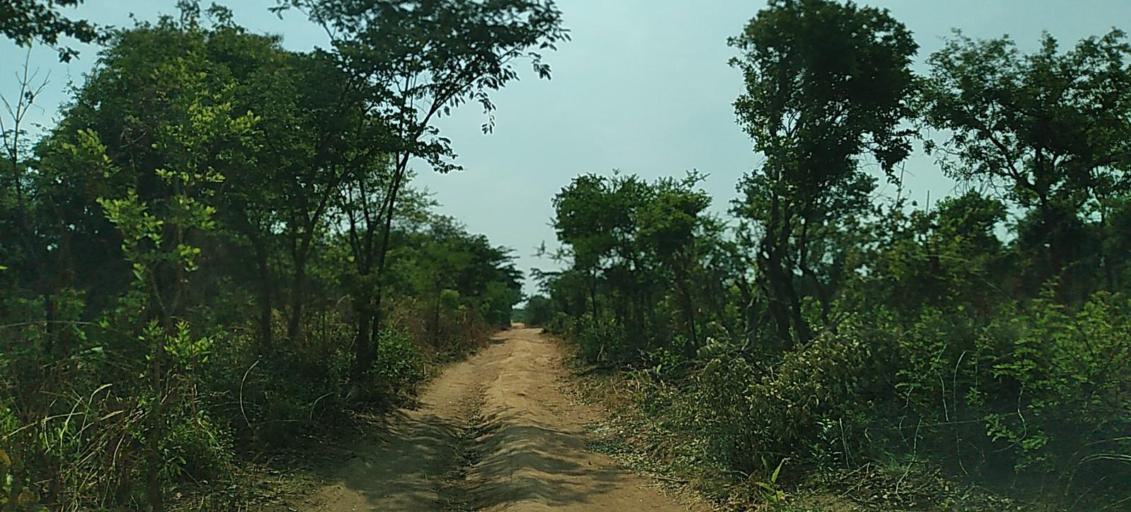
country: ZM
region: Copperbelt
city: Ndola
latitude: -13.2101
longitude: 28.7419
